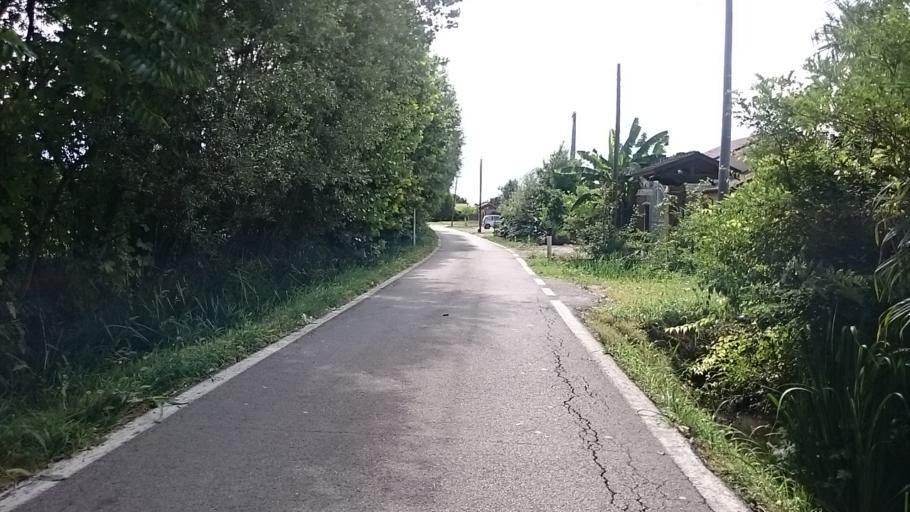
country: IT
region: Veneto
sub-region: Provincia di Padova
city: Albignasego
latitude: 45.3464
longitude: 11.8914
